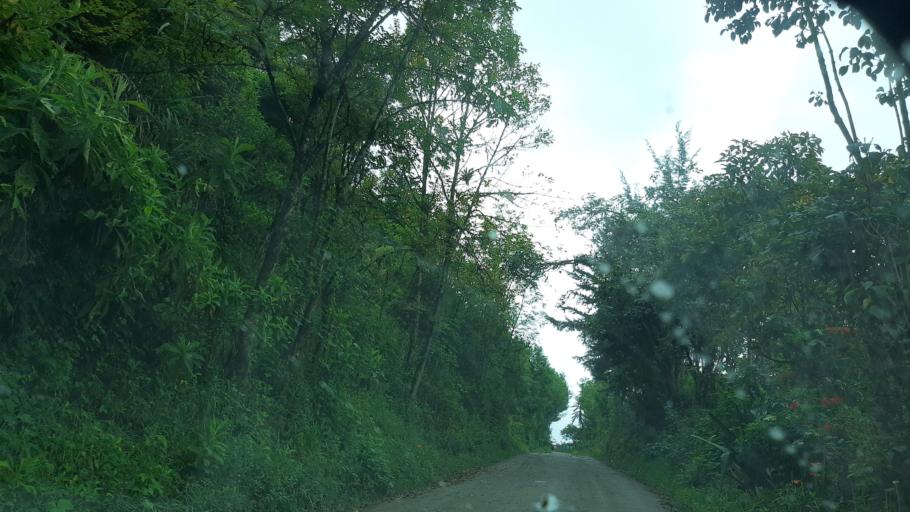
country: CO
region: Boyaca
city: Guateque
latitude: 5.0329
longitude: -73.4462
